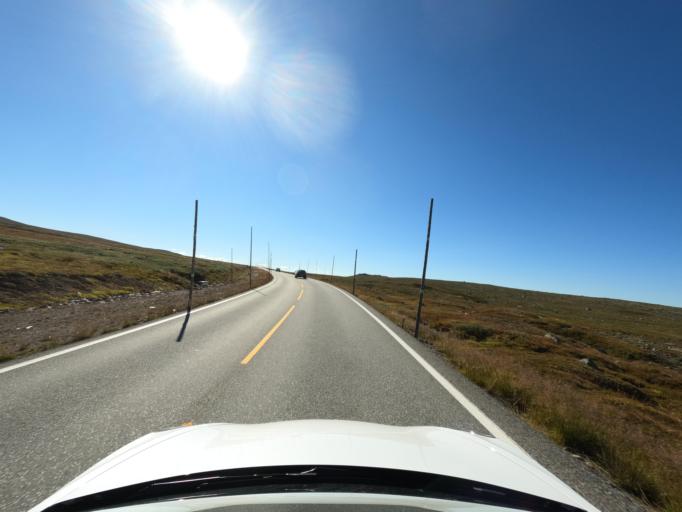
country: NO
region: Hordaland
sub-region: Eidfjord
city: Eidfjord
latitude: 60.3900
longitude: 7.5960
